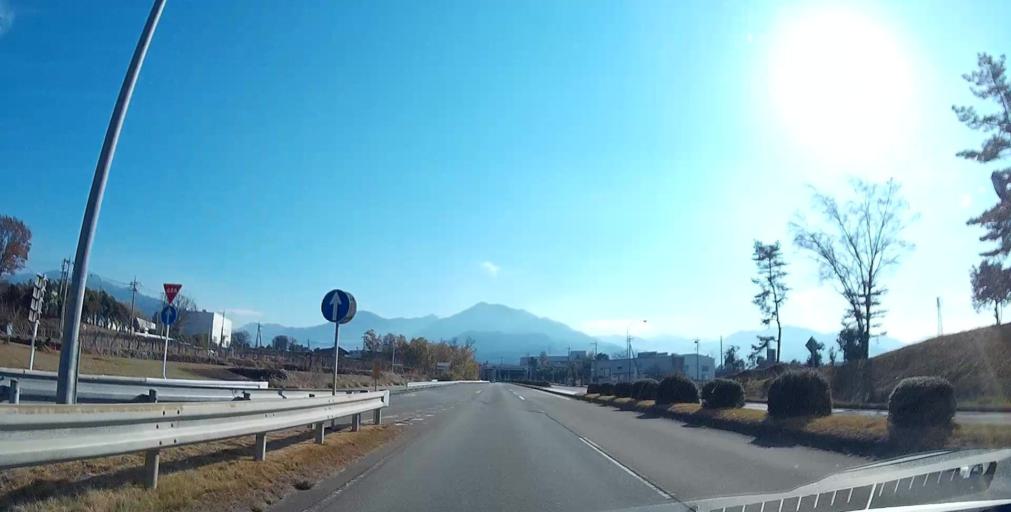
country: JP
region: Yamanashi
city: Isawa
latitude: 35.6365
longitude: 138.6729
